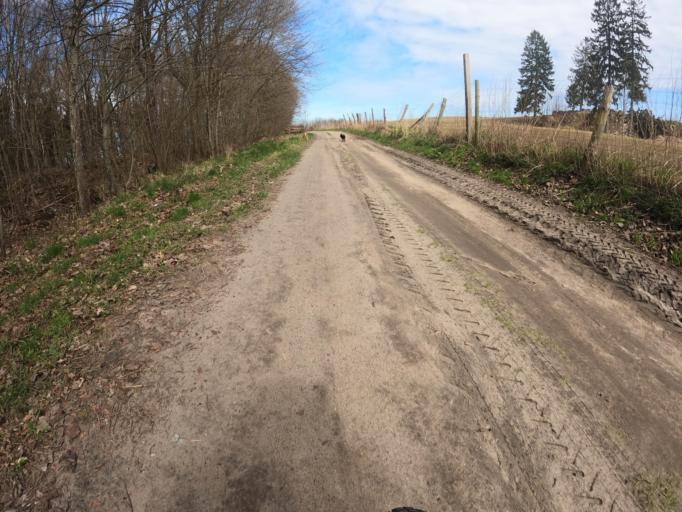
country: PL
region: West Pomeranian Voivodeship
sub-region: Powiat gryficki
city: Brojce
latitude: 53.9629
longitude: 15.3747
